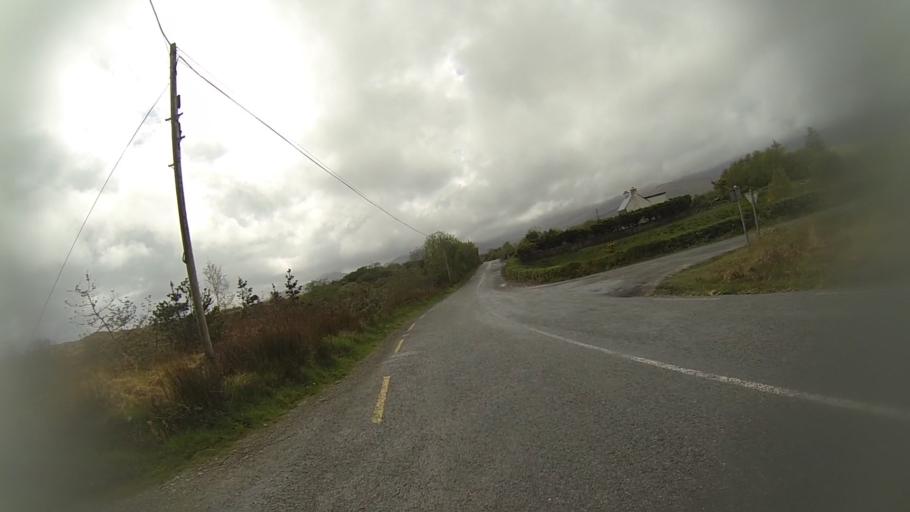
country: IE
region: Munster
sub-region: Ciarrai
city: Killorglin
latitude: 51.8513
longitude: -9.8802
